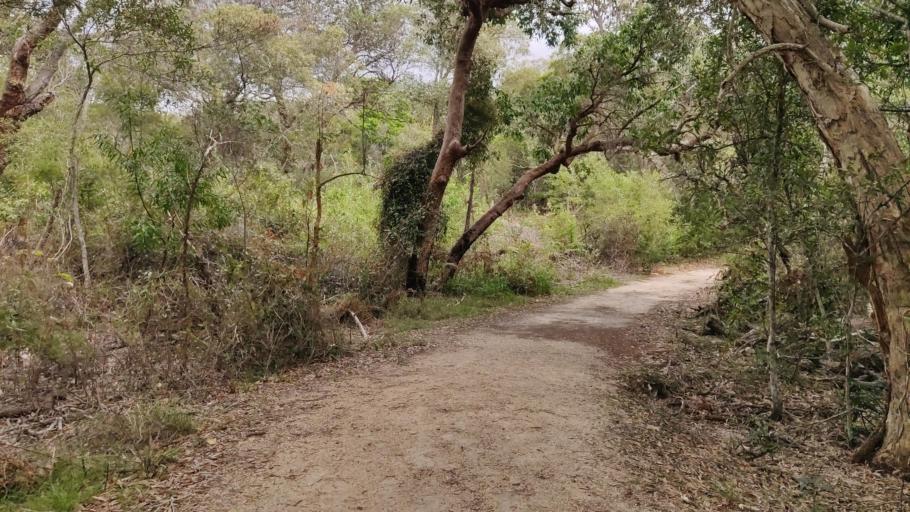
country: AU
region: New South Wales
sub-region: Port Macquarie-Hastings
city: North Haven
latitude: -31.6421
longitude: 152.8376
